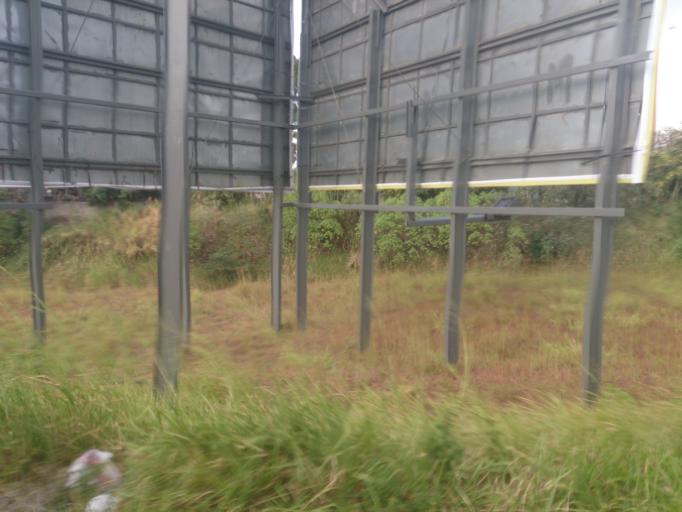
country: CR
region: San Jose
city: San Rafael
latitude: 9.9339
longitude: -84.1121
